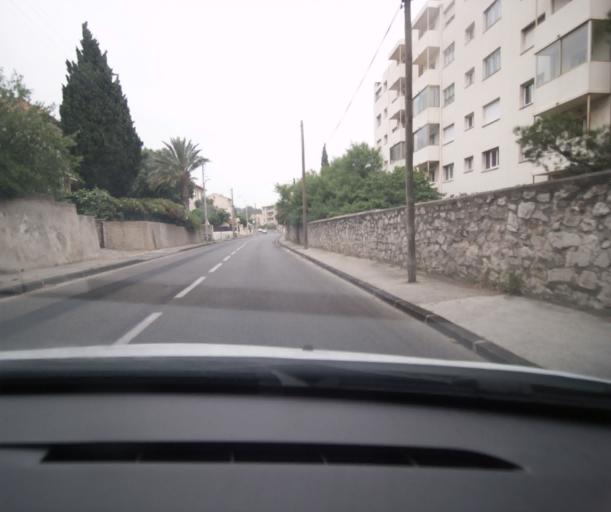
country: FR
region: Provence-Alpes-Cote d'Azur
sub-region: Departement du Var
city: Toulon
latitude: 43.1356
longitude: 5.9292
